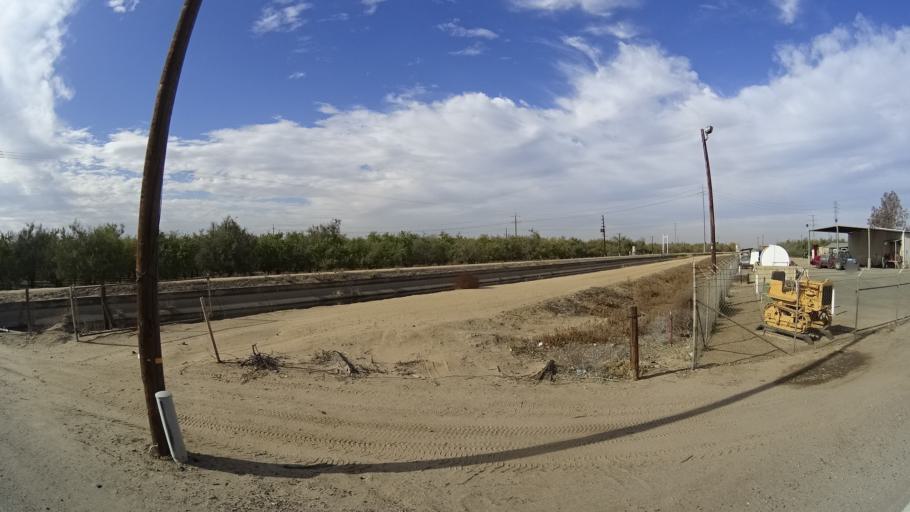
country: US
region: California
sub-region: Kern County
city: Greenacres
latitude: 35.4390
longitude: -119.0921
